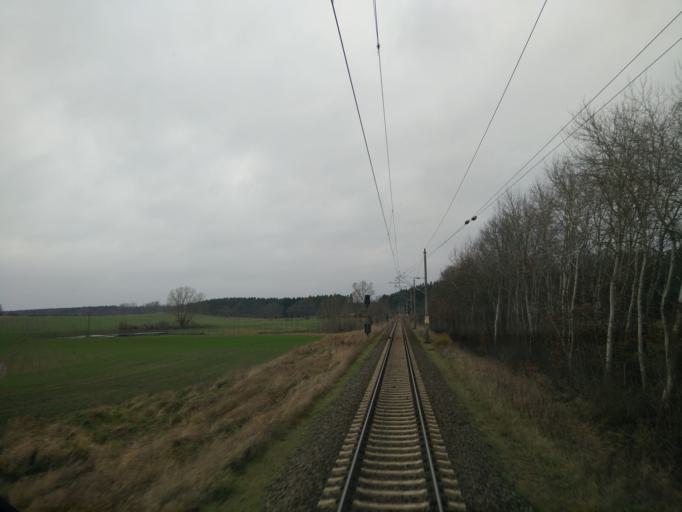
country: DE
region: Mecklenburg-Vorpommern
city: Bad Kleinen
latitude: 53.7828
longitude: 11.4870
